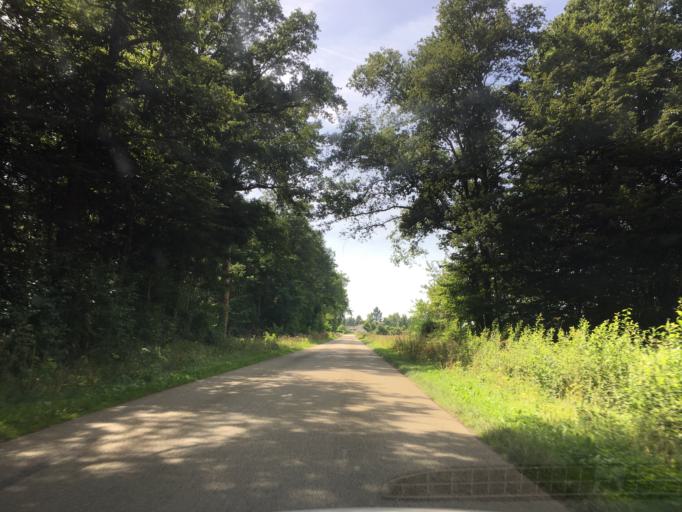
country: FR
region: Bourgogne
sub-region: Departement de l'Yonne
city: Charbuy
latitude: 47.7998
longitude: 3.4502
